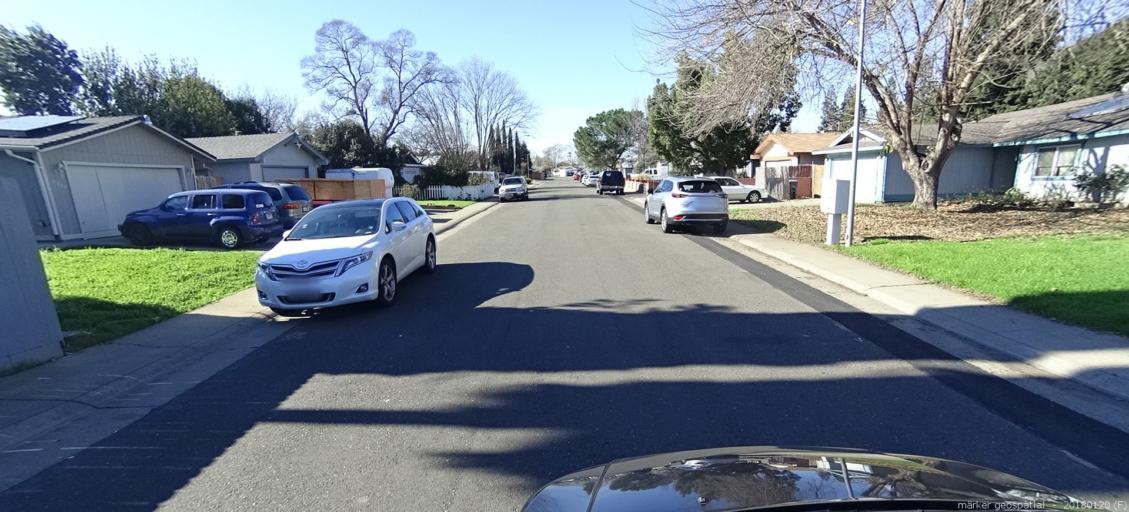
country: US
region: California
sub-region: Sacramento County
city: La Riviera
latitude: 38.5604
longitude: -121.3282
